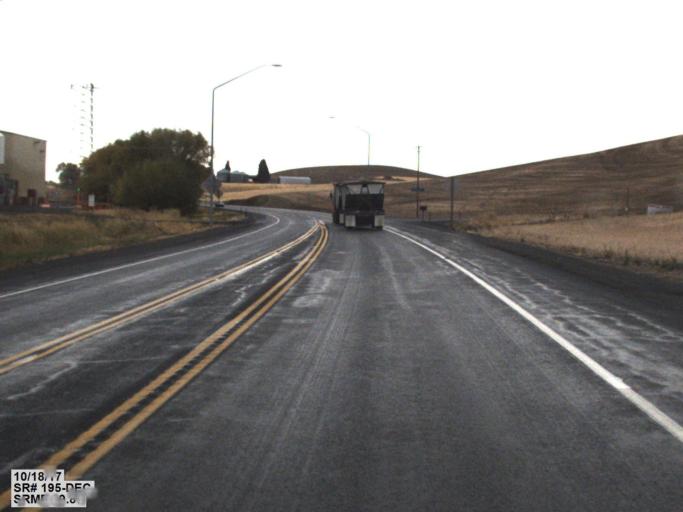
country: US
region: Washington
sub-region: Whitman County
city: Pullman
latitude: 46.7068
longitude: -117.2041
